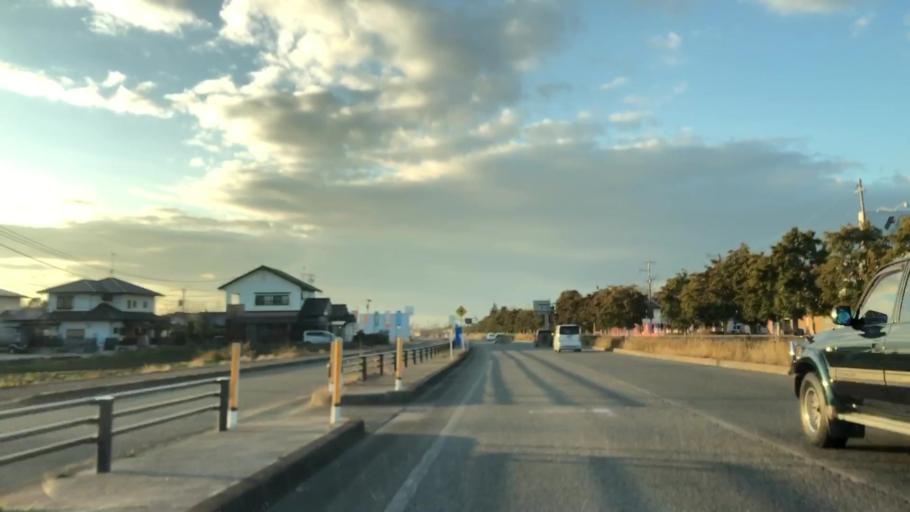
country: JP
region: Fukuoka
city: Nakatsu
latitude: 33.5581
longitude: 131.2009
